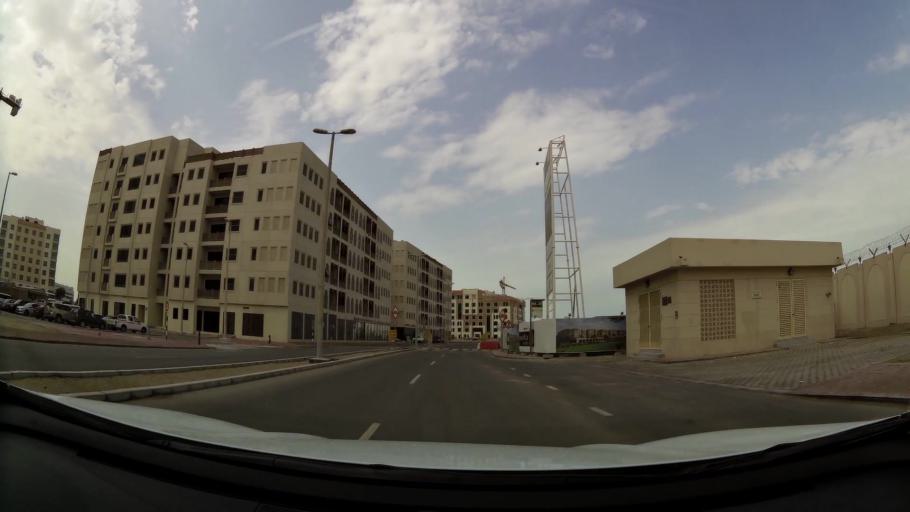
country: AE
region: Abu Dhabi
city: Abu Dhabi
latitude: 24.4199
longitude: 54.4656
